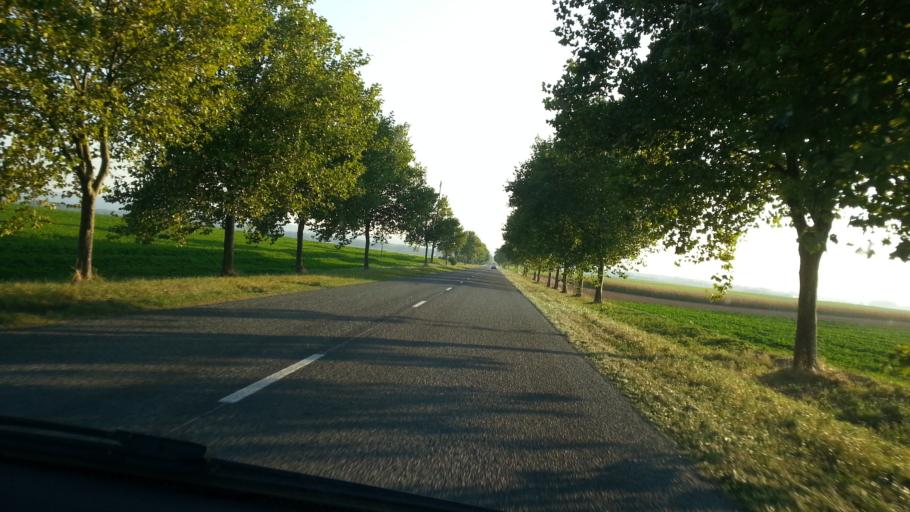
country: FR
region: Picardie
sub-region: Departement de l'Oise
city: Saint-Martin-Longueau
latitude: 49.3674
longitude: 2.6146
